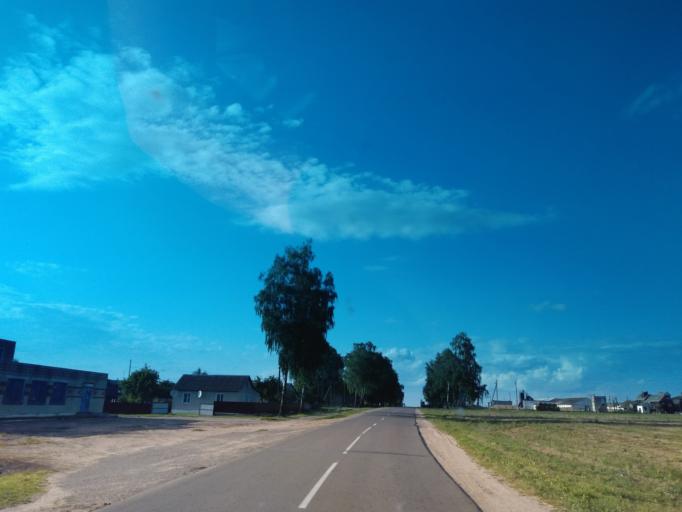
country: BY
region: Minsk
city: Kapyl'
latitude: 53.2601
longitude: 26.9577
